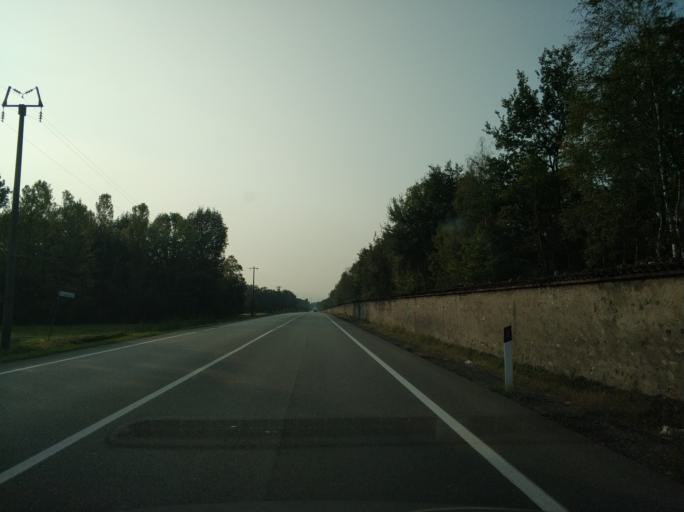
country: IT
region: Piedmont
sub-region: Provincia di Torino
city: Robassomero
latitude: 45.2022
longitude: 7.5549
